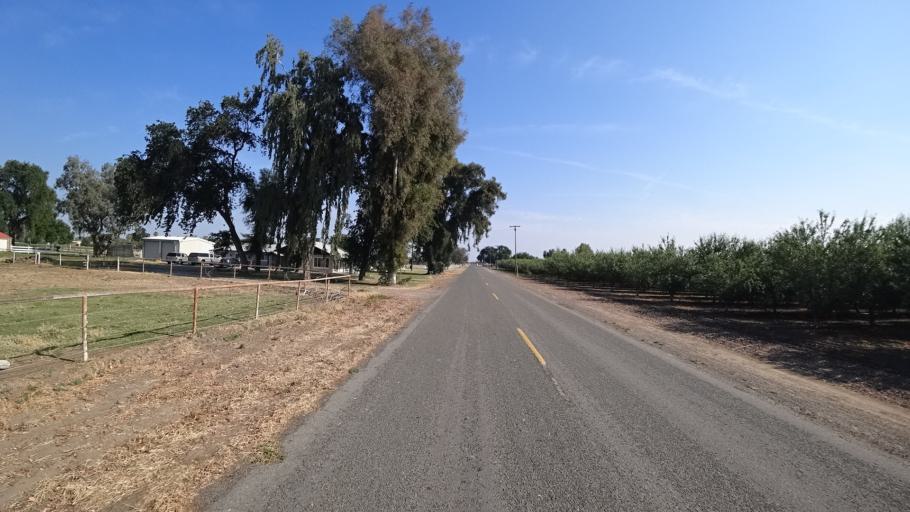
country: US
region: California
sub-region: Kings County
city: Lemoore
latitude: 36.3566
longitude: -119.8340
